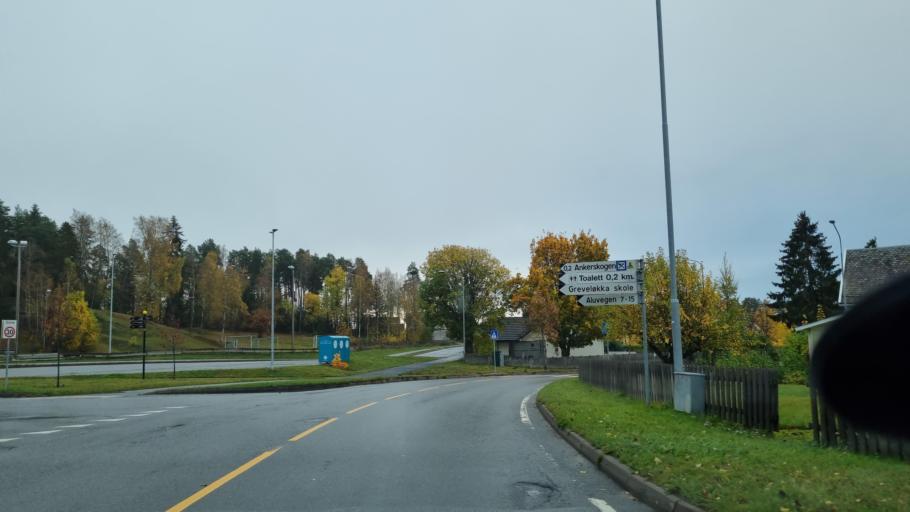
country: NO
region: Hedmark
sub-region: Hamar
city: Hamar
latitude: 60.8027
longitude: 11.0632
